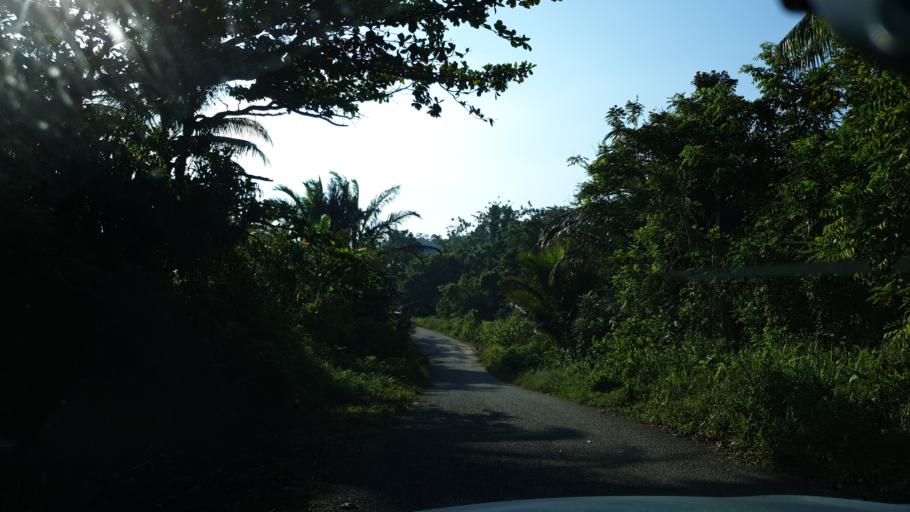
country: PG
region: East Sepik
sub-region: Wewak
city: Wewak
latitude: -3.6919
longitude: 143.6563
